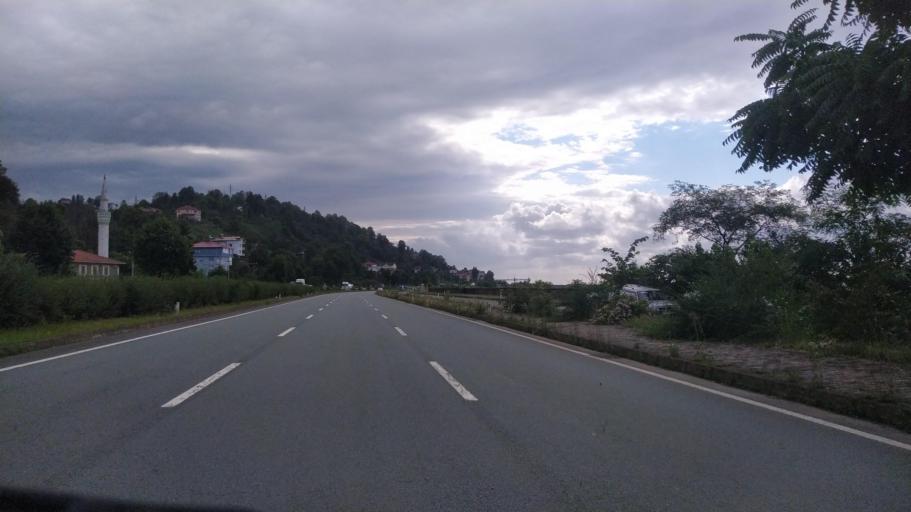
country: TR
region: Rize
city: Ardesen
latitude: 41.2114
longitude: 41.0466
